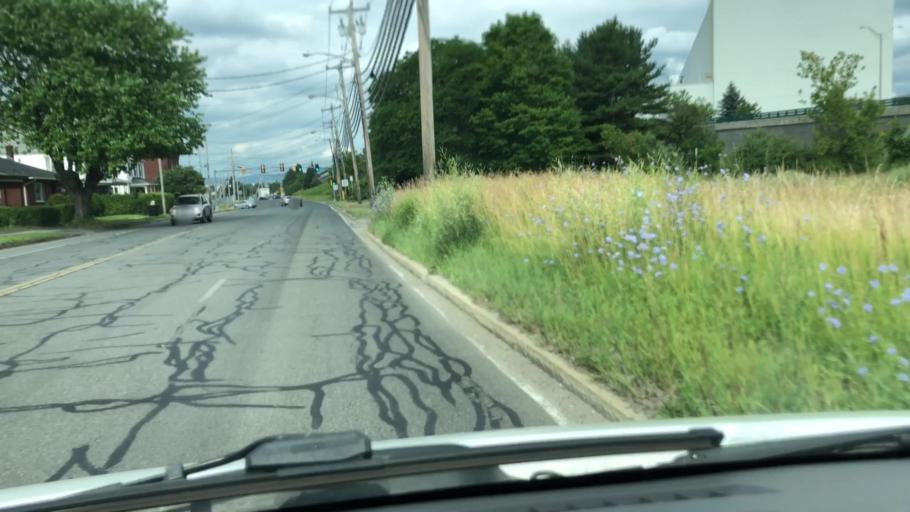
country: US
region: Massachusetts
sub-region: Berkshire County
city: Pittsfield
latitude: 42.4533
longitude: -73.2247
